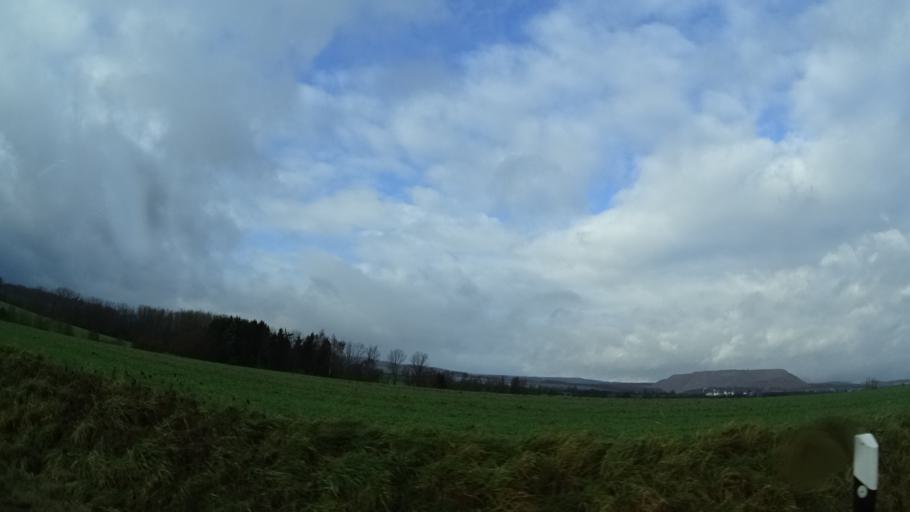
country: DE
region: Hesse
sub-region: Regierungsbezirk Kassel
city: Neuhof
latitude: 50.4305
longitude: 9.6062
